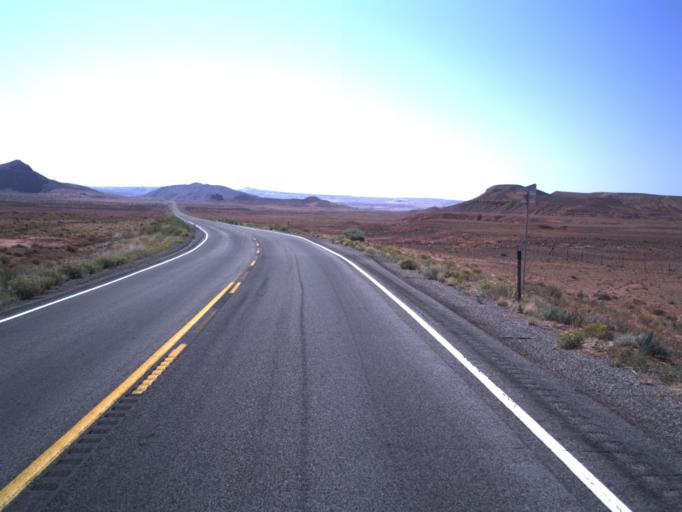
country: US
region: Utah
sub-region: San Juan County
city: Blanding
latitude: 37.0121
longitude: -109.6124
